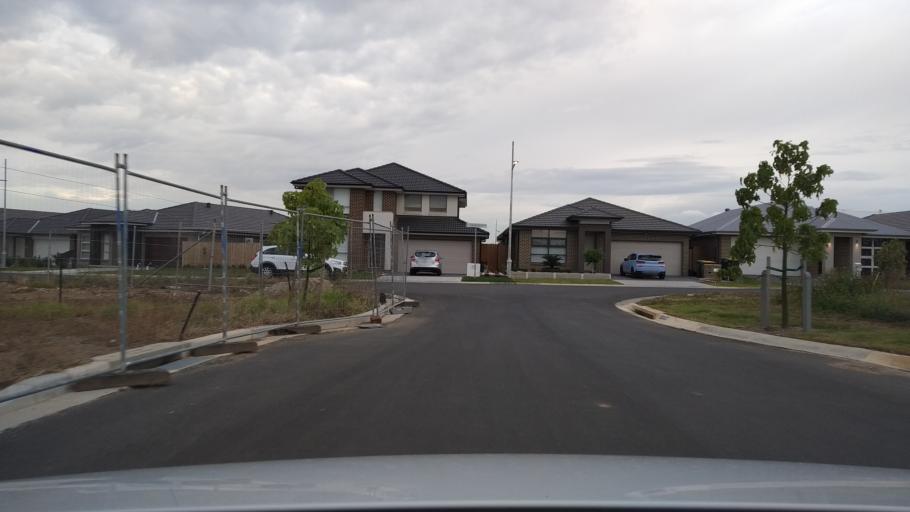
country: AU
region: New South Wales
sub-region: Camden
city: Narellan
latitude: -33.9978
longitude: 150.7258
